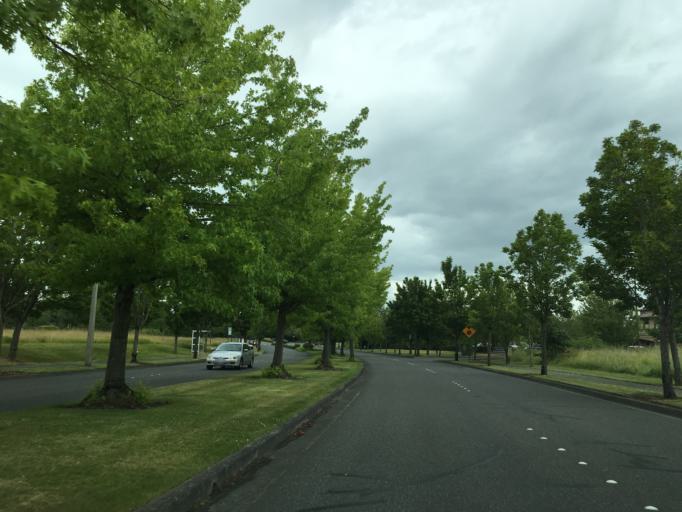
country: US
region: Washington
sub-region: Whatcom County
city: Bellingham
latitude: 48.8043
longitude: -122.4956
